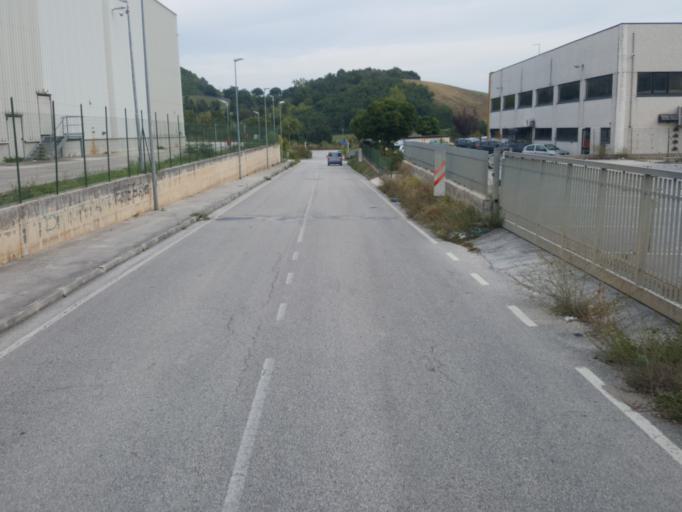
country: IT
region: The Marches
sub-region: Provincia di Ancona
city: Fabriano
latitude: 43.3437
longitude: 12.8622
